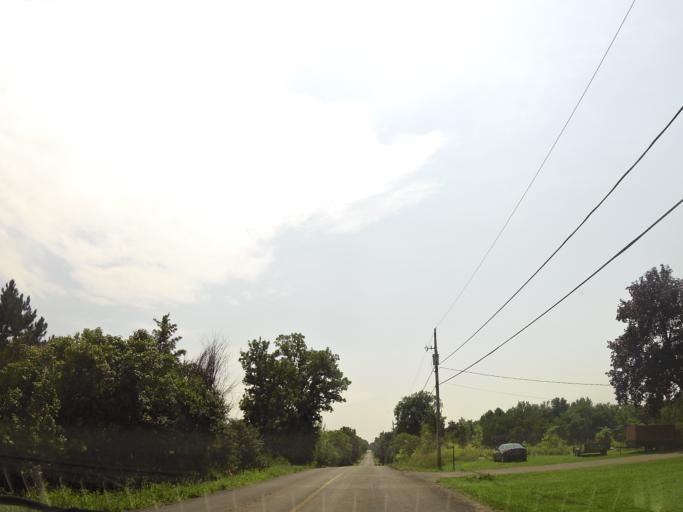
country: CA
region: Ontario
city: Kingston
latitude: 44.4308
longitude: -76.5910
